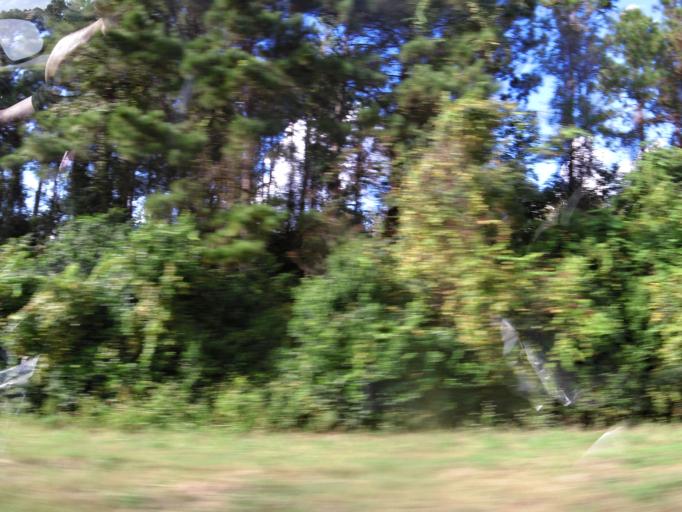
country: US
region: Georgia
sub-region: Brooks County
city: Quitman
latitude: 30.7850
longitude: -83.6209
